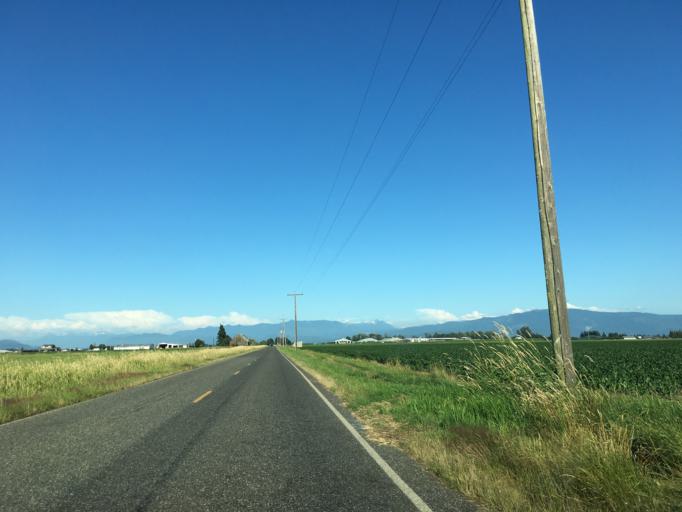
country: US
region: Washington
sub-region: Whatcom County
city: Lynden
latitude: 48.9863
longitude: -122.4718
